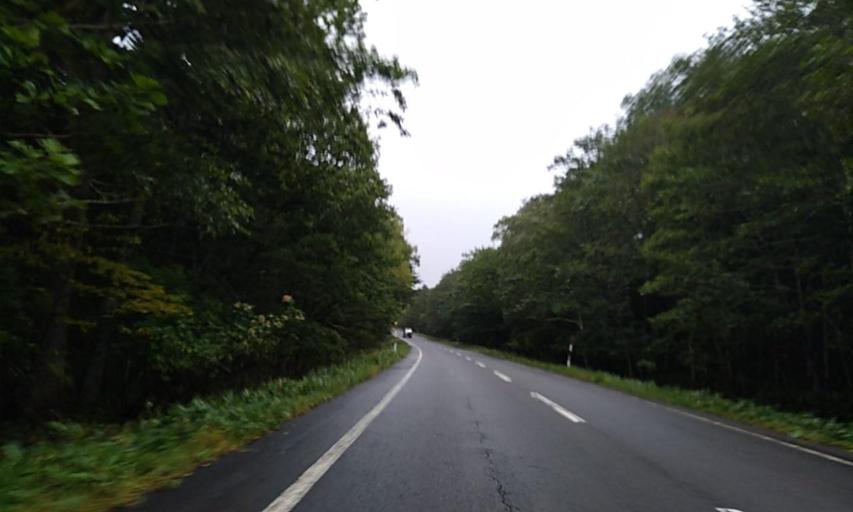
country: JP
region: Hokkaido
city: Bihoro
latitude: 43.5319
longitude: 144.5012
